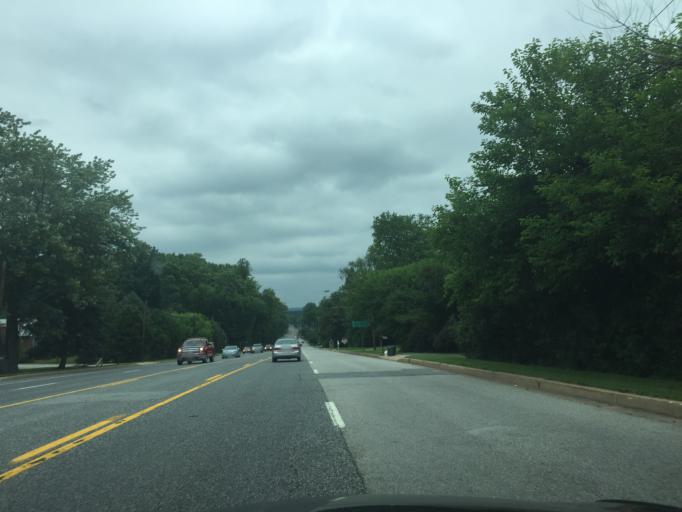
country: US
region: Maryland
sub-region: Baltimore County
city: Towson
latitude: 39.4165
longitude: -76.5995
